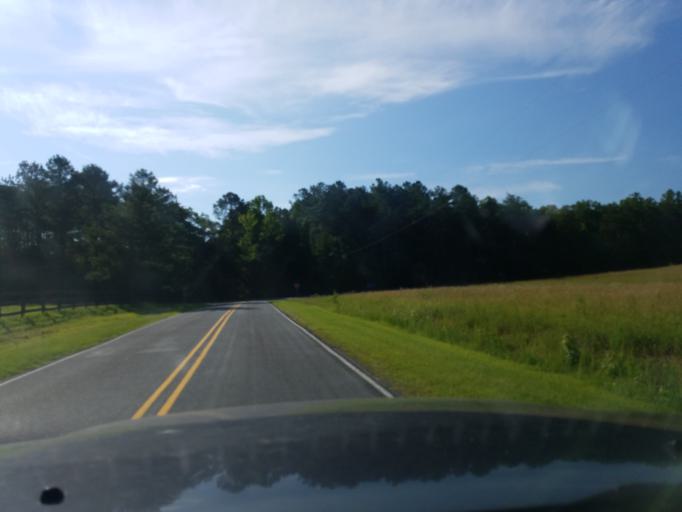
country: US
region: North Carolina
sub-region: Granville County
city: Butner
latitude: 36.1923
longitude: -78.8239
